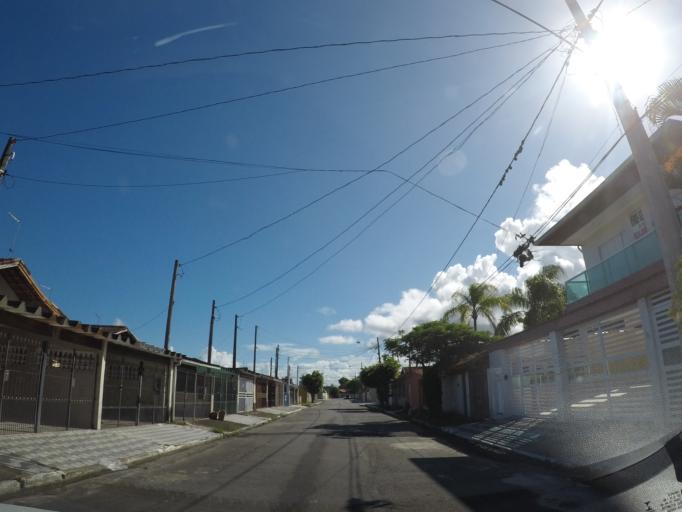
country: BR
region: Sao Paulo
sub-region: Mongagua
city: Mongagua
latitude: -24.0607
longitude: -46.5564
